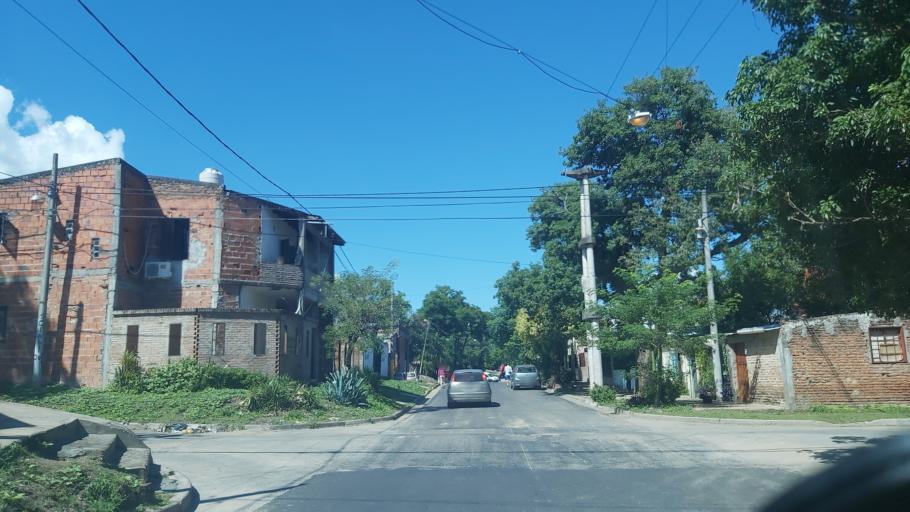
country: AR
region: Corrientes
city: Corrientes
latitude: -27.4827
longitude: -58.8480
